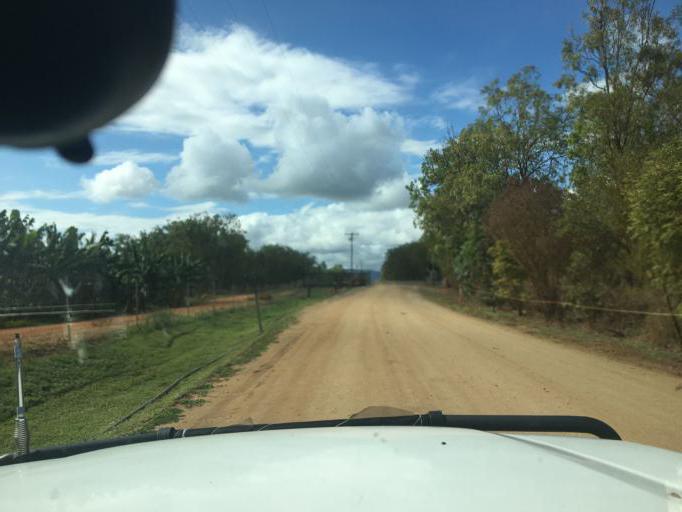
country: AU
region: Queensland
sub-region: Tablelands
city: Mareeba
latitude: -17.0979
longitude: 145.4120
